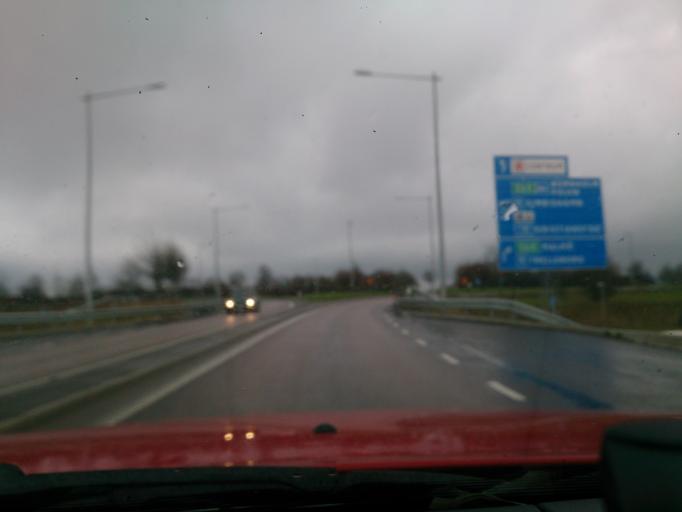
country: SE
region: Skane
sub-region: Ystads Kommun
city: Ystad
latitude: 55.4439
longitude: 13.8066
